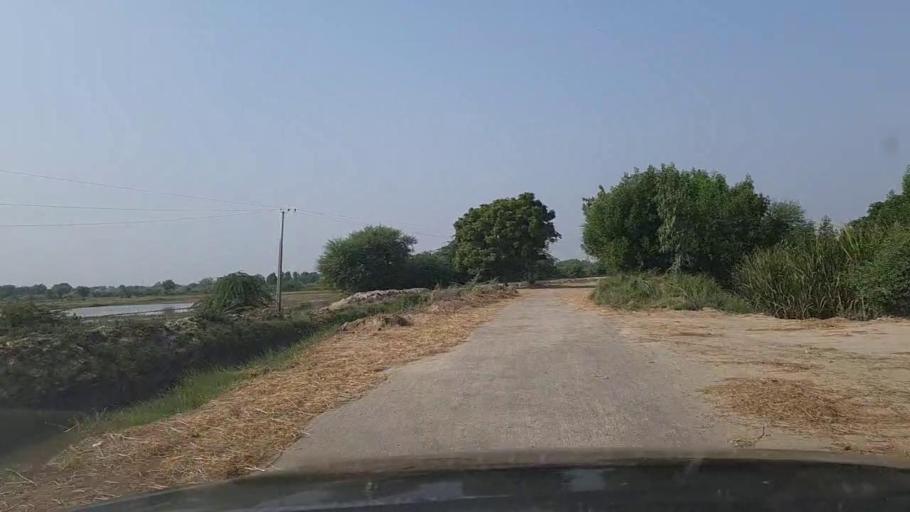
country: PK
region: Sindh
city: Mirpur Batoro
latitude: 24.7044
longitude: 68.2548
